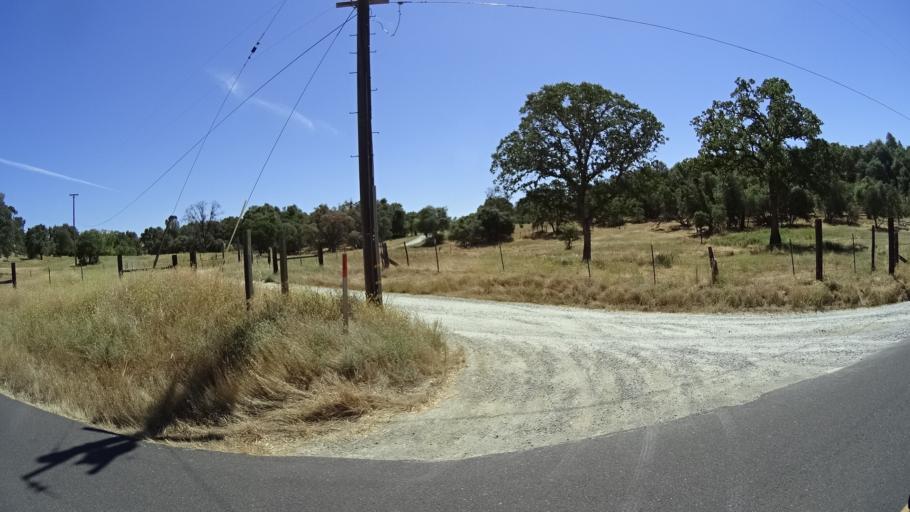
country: US
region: California
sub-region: Calaveras County
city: Angels Camp
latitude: 38.0896
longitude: -120.5563
